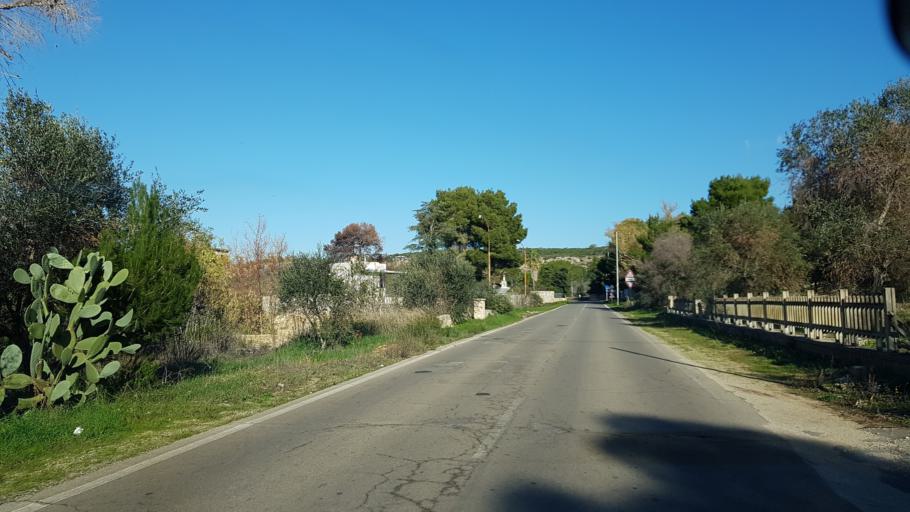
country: IT
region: Apulia
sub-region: Provincia di Lecce
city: Sannicola
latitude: 40.1007
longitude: 18.0199
